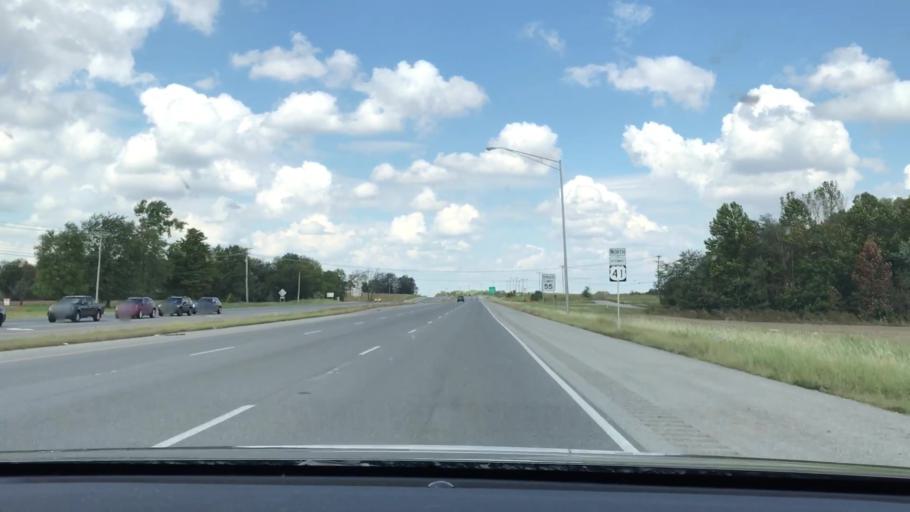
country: US
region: Kentucky
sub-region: Christian County
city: Oak Grove
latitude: 36.6767
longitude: -87.4464
